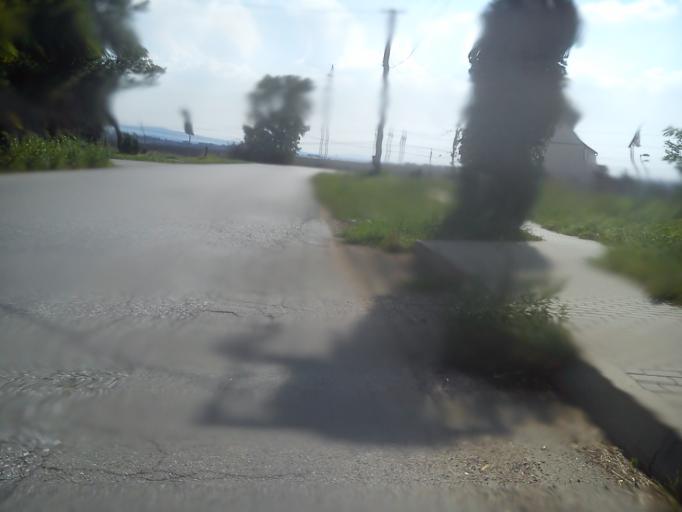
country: CZ
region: South Moravian
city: Sokolnice
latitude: 49.1084
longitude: 16.7293
